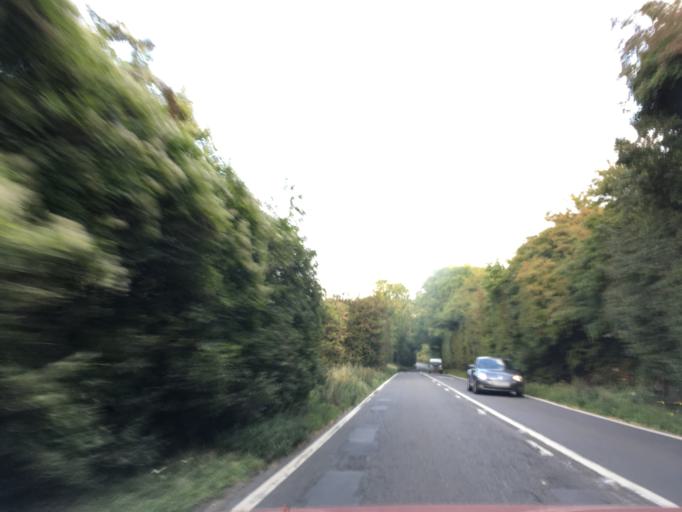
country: GB
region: England
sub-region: Gloucestershire
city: Northleach
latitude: 51.8541
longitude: -1.8077
